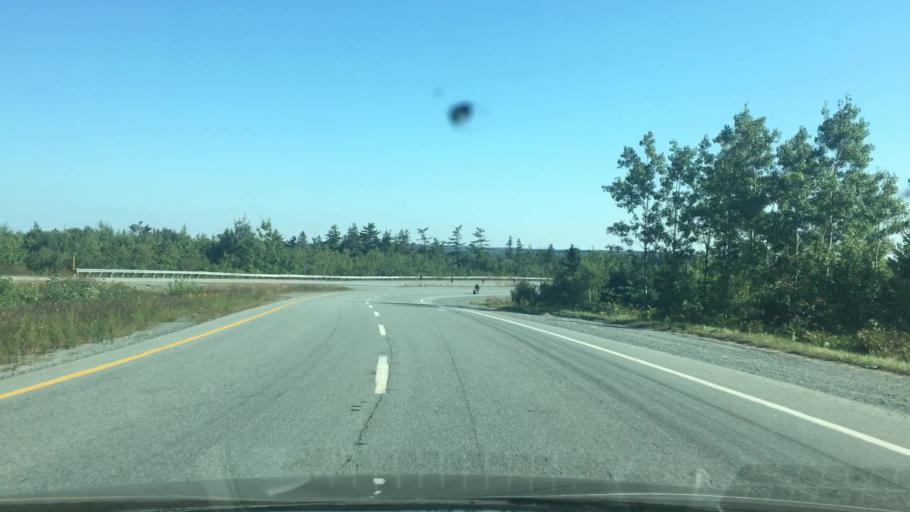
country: CA
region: Nova Scotia
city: Dartmouth
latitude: 44.7223
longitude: -63.5794
